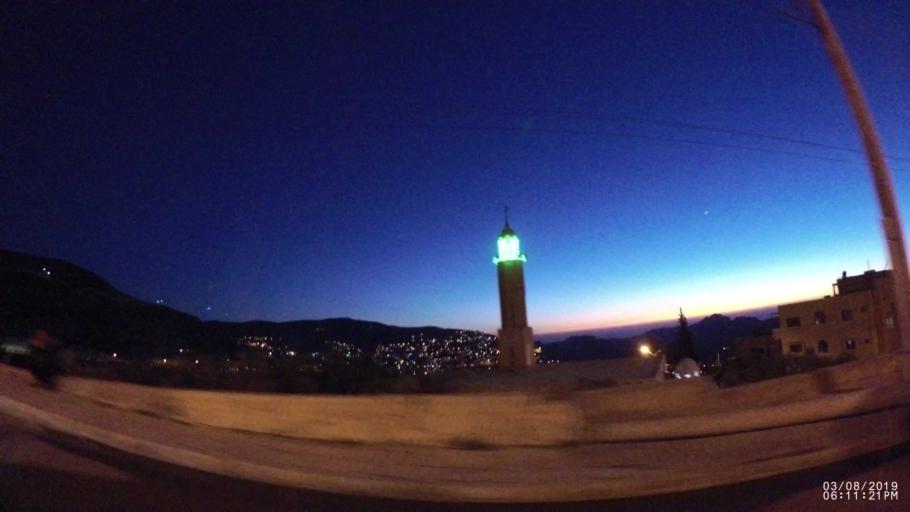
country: JO
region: Ma'an
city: Petra
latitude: 30.3295
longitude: 35.4896
